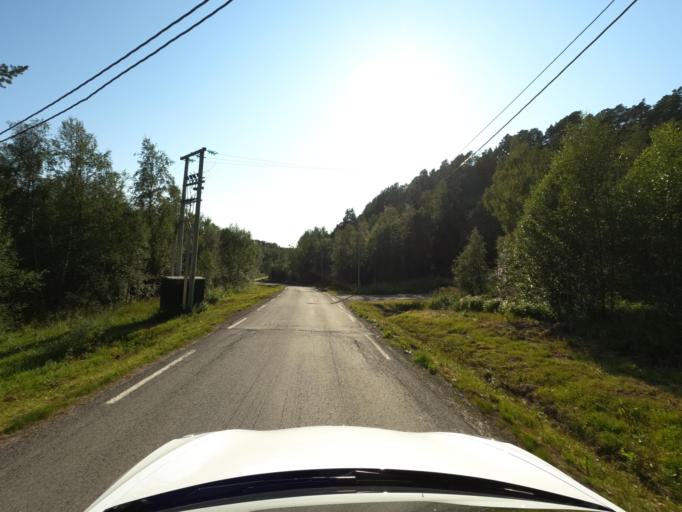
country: NO
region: Nordland
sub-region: Narvik
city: Bjerkvik
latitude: 68.4752
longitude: 17.5111
